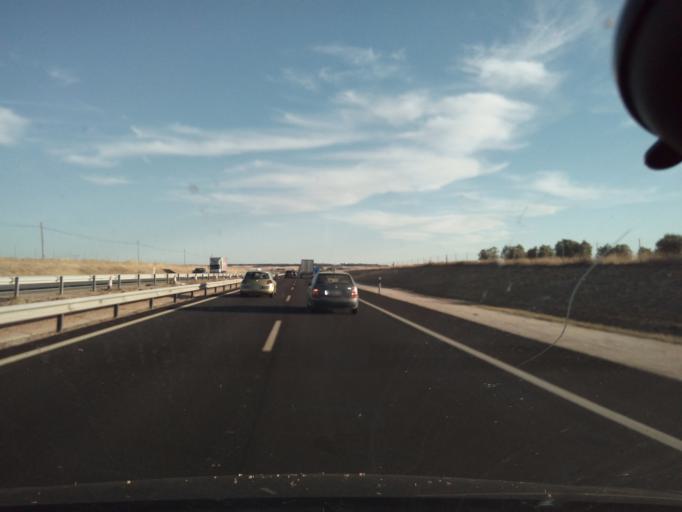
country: ES
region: Castille-La Mancha
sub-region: Province of Toledo
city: Tembleque
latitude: 39.7136
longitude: -3.4955
